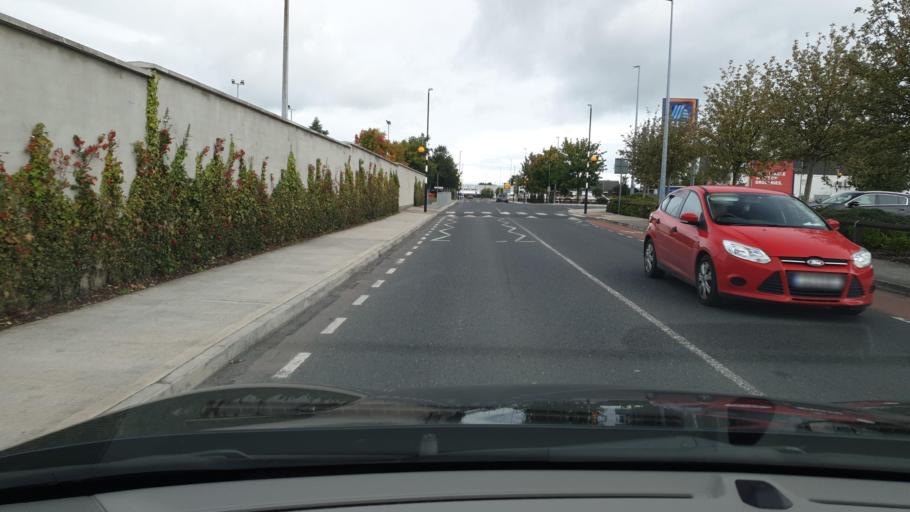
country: IE
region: Leinster
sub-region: Laois
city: Portlaoise
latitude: 53.0302
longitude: -7.2994
